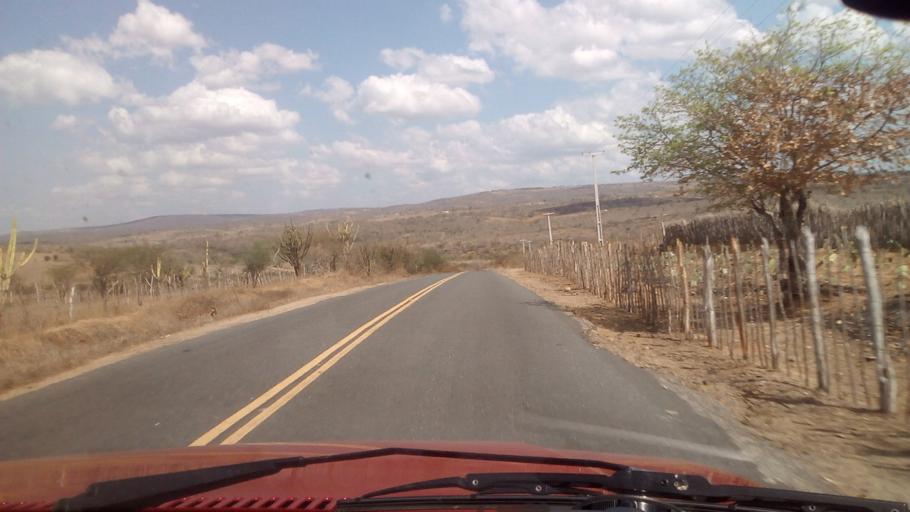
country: BR
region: Paraiba
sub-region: Cacimba De Dentro
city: Cacimba de Dentro
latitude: -6.6745
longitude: -35.7486
